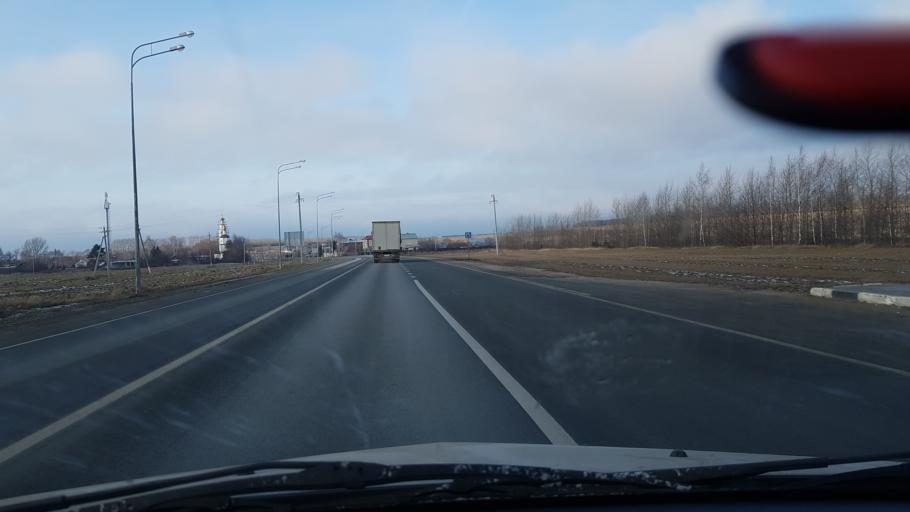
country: RU
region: Tatarstan
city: Laishevo
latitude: 55.3913
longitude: 49.8084
